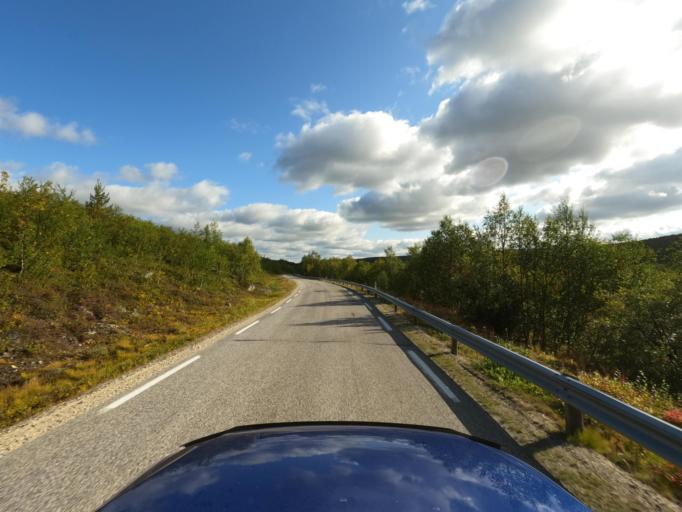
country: NO
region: Finnmark Fylke
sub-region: Porsanger
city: Lakselv
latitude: 69.4219
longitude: 24.8087
